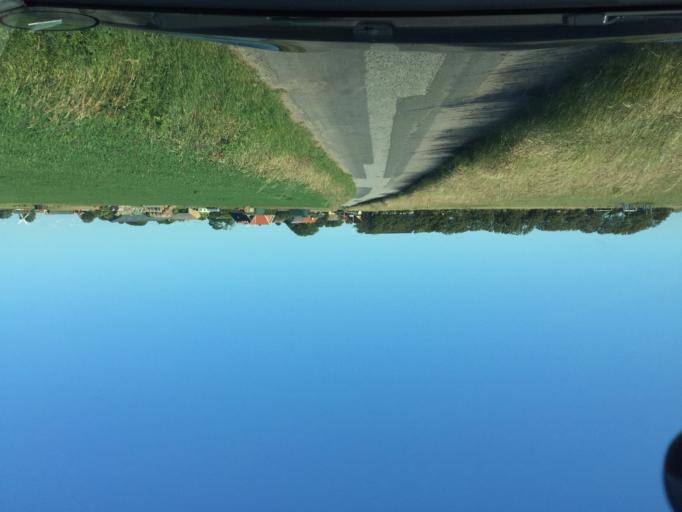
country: DK
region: Zealand
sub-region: Slagelse Kommune
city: Skaelskor
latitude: 55.2079
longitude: 11.1857
